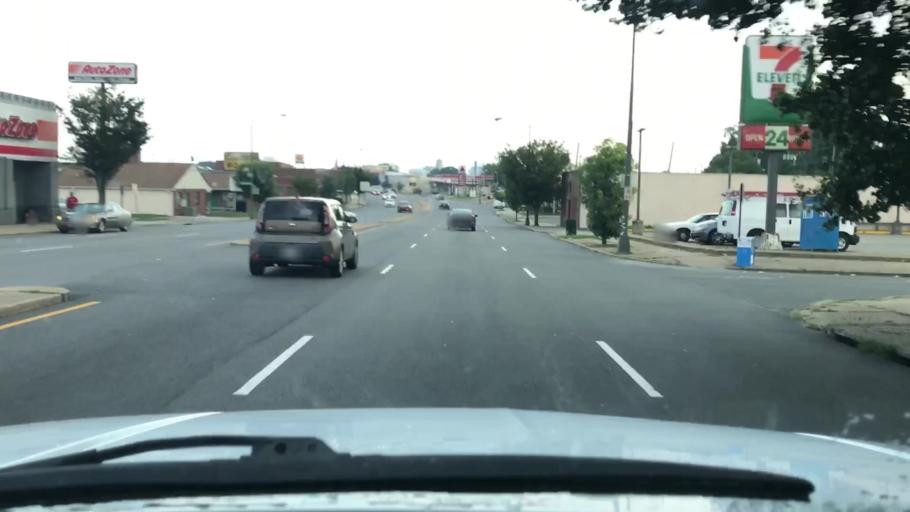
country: US
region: Virginia
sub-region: City of Richmond
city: Richmond
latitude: 37.5649
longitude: -77.4441
